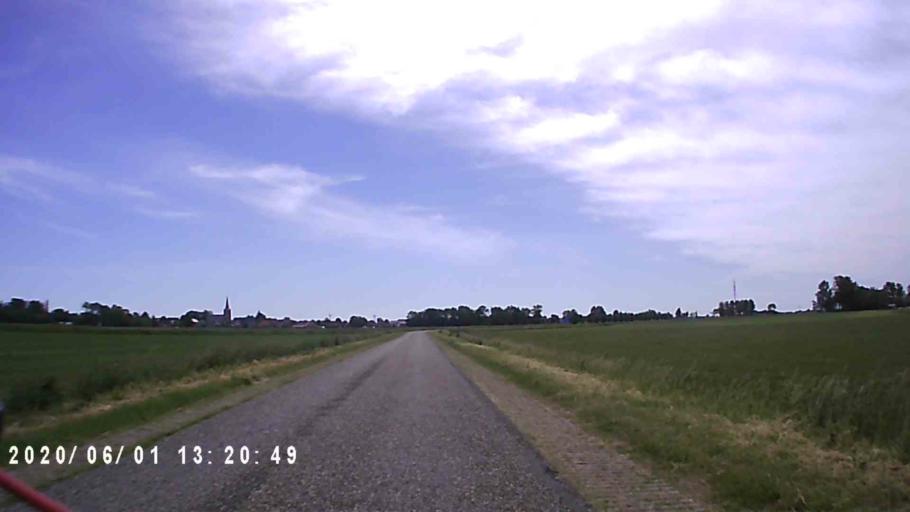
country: NL
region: Friesland
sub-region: Gemeente Littenseradiel
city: Wommels
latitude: 53.1136
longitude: 5.5826
